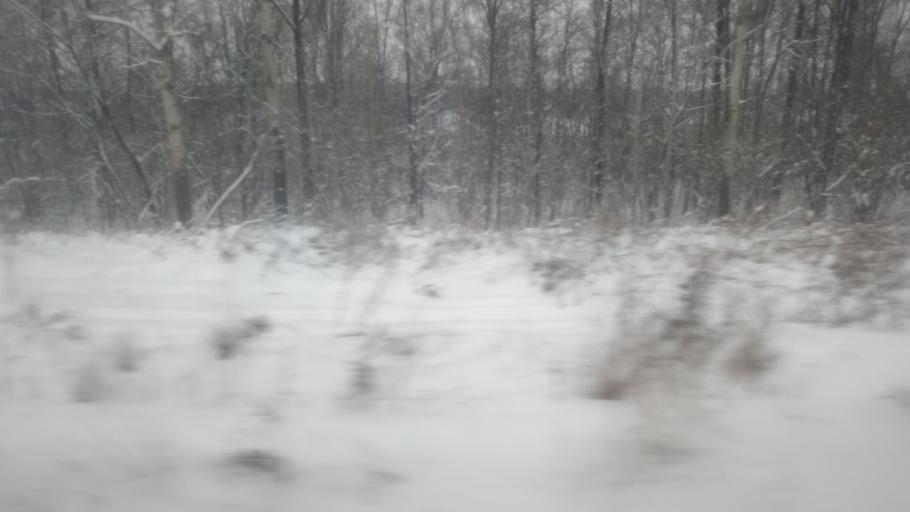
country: RU
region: Udmurtiya
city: Sigayevo
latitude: 56.4525
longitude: 53.7028
